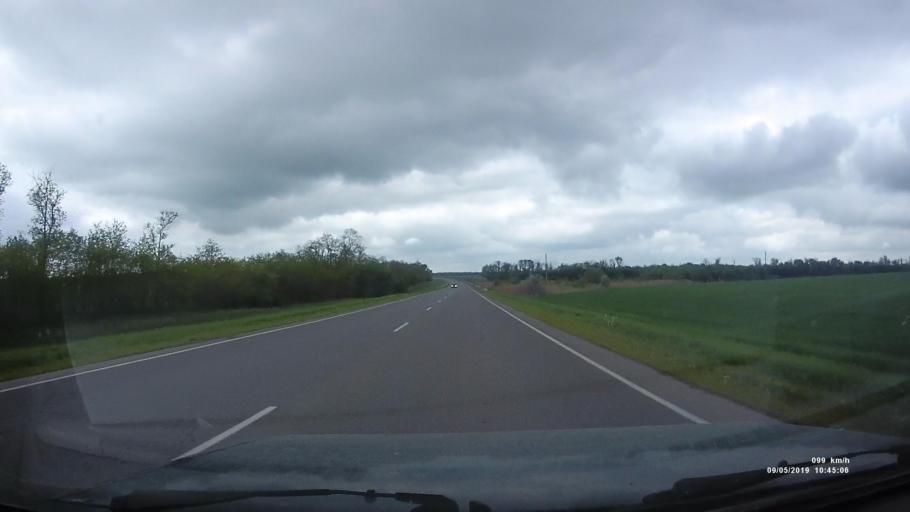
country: RU
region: Rostov
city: Peshkovo
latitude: 46.9975
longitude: 39.3747
